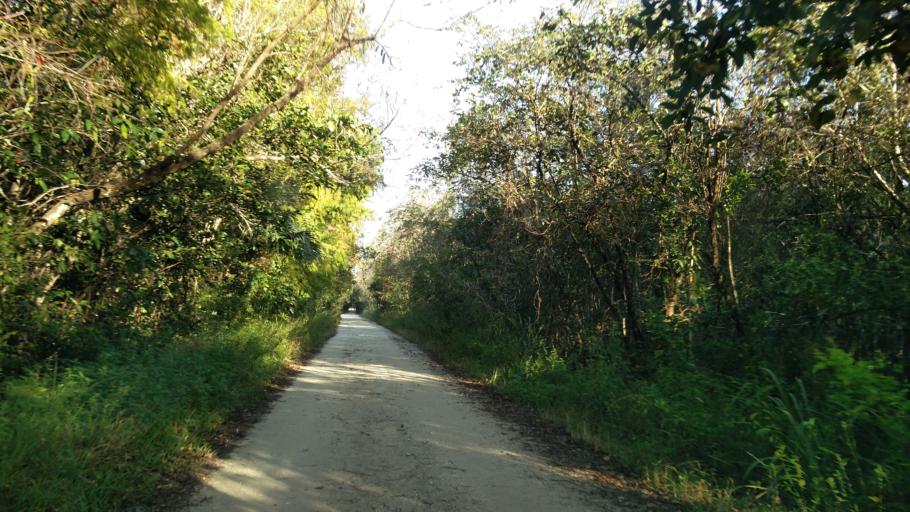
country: US
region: Florida
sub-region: Collier County
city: Lely Resort
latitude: 25.9800
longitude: -81.4025
